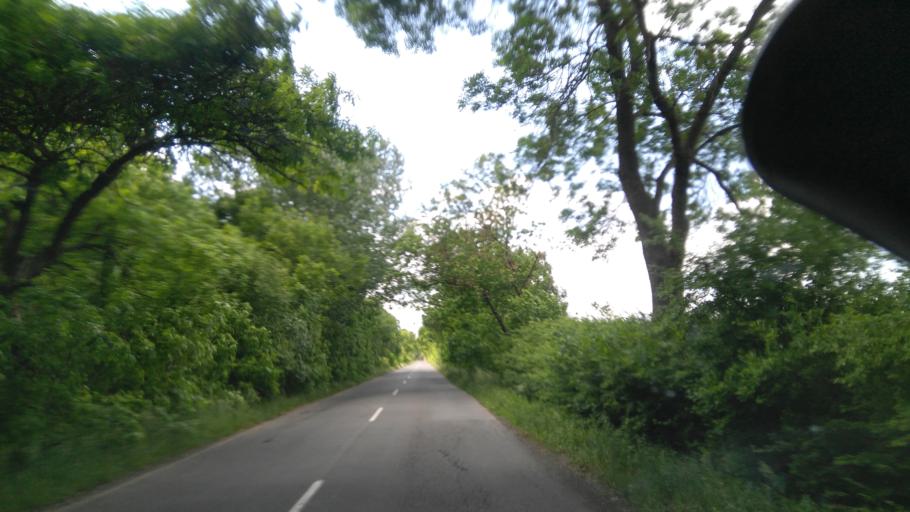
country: HU
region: Bekes
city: Bucsa
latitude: 47.1826
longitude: 21.0453
